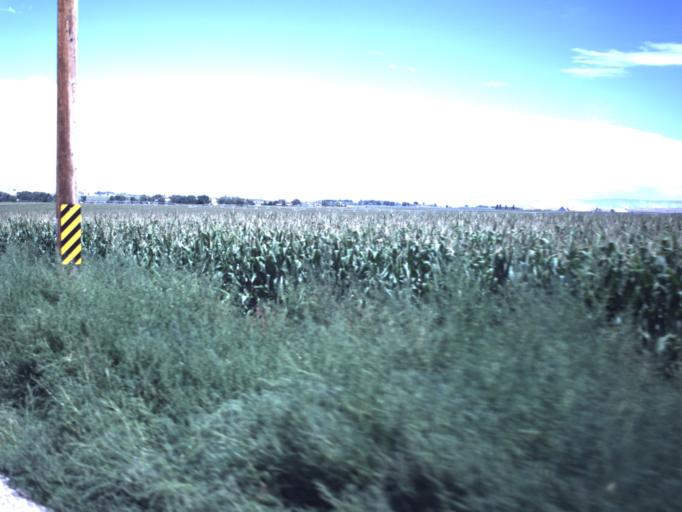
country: US
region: Utah
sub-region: Uintah County
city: Naples
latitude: 40.1762
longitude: -109.6645
